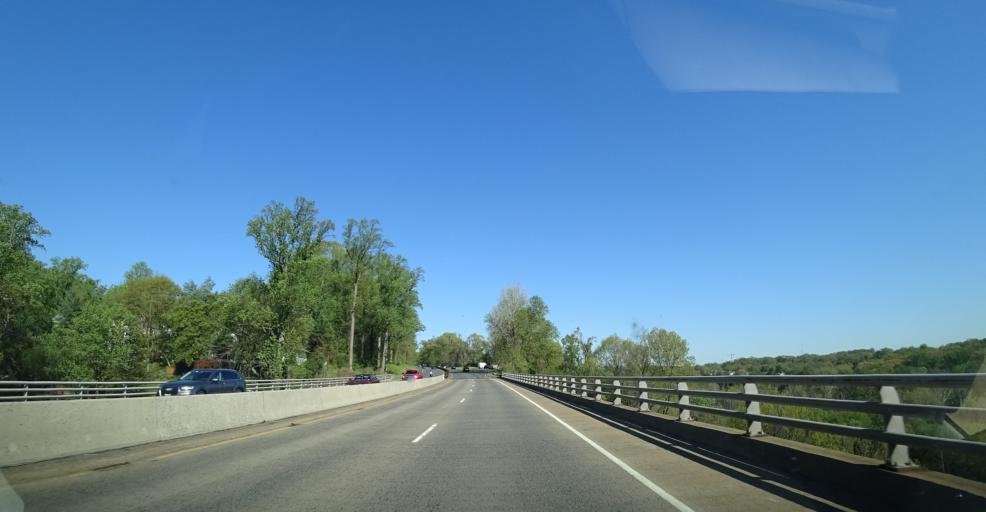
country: US
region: Maryland
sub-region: Montgomery County
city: Brookmont
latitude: 38.9196
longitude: -77.1080
